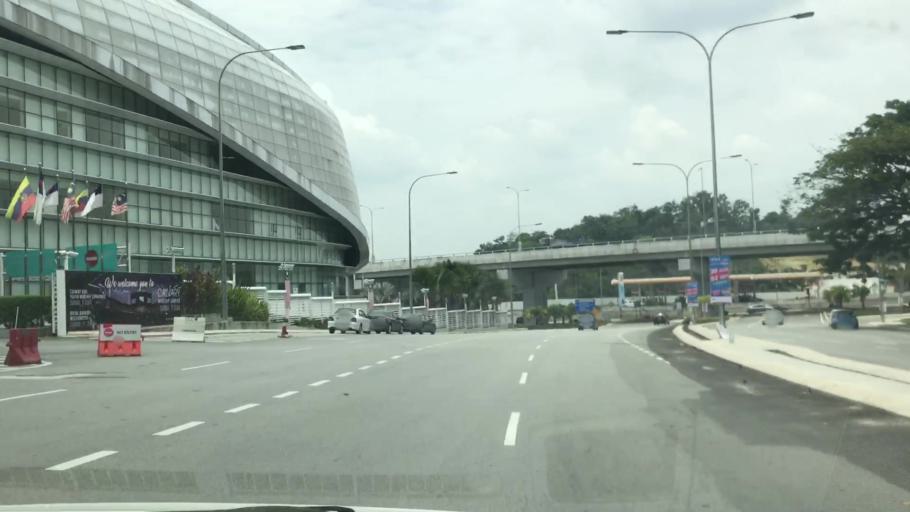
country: MY
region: Selangor
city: Kampong Baharu Balakong
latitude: 3.0510
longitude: 101.6798
